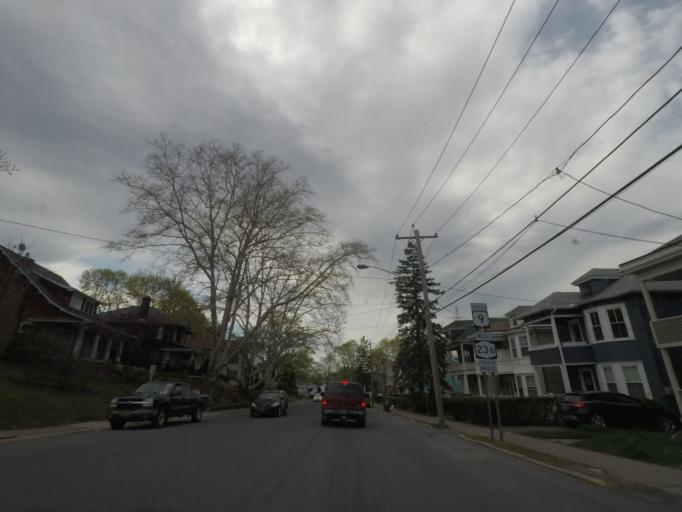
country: US
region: New York
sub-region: Columbia County
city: Oakdale
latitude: 42.2479
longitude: -73.7737
